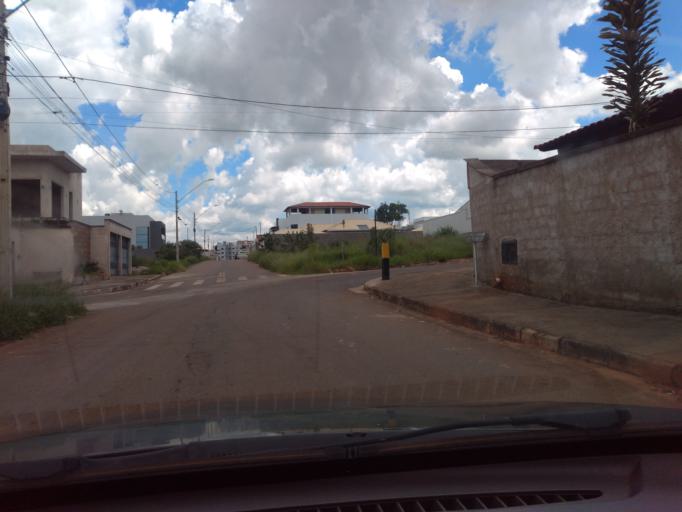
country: BR
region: Minas Gerais
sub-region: Tres Coracoes
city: Tres Coracoes
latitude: -21.6783
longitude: -45.2662
